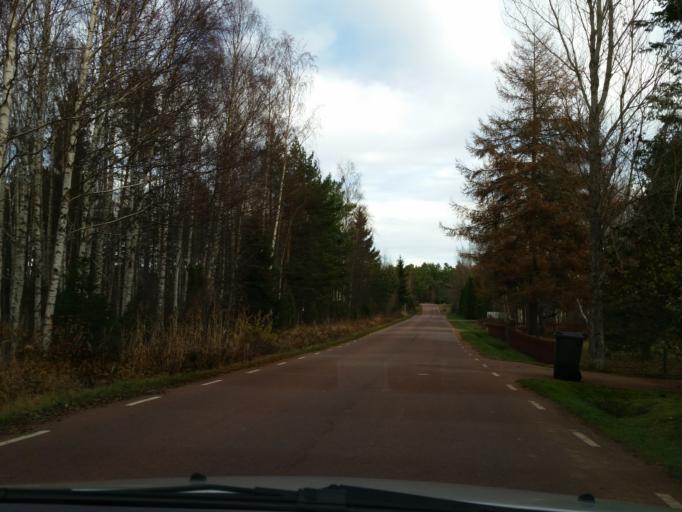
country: AX
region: Alands landsbygd
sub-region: Finstroem
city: Finstroem
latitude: 60.2356
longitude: 19.9712
